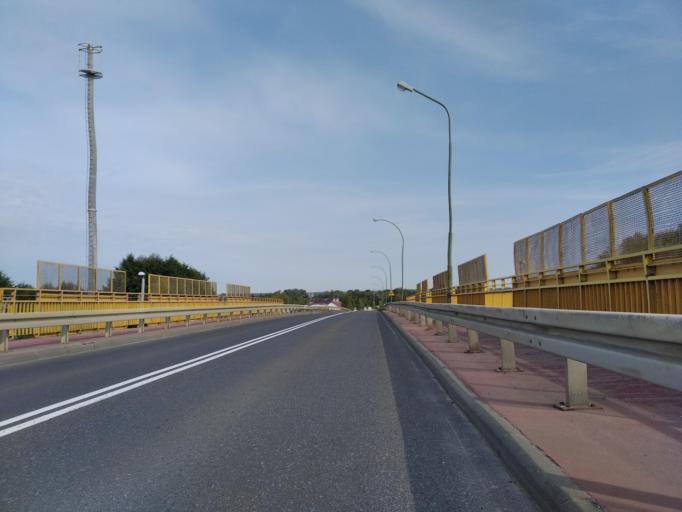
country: PL
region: Subcarpathian Voivodeship
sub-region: Powiat ropczycko-sedziszowski
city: Ostrow
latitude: 50.0784
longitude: 21.5835
